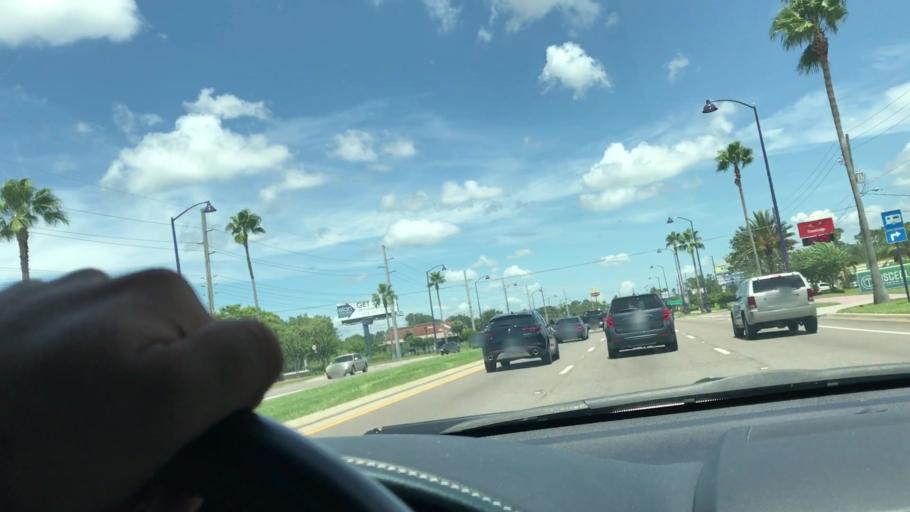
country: US
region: Florida
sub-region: Osceola County
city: Kissimmee
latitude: 28.3154
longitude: -81.4683
